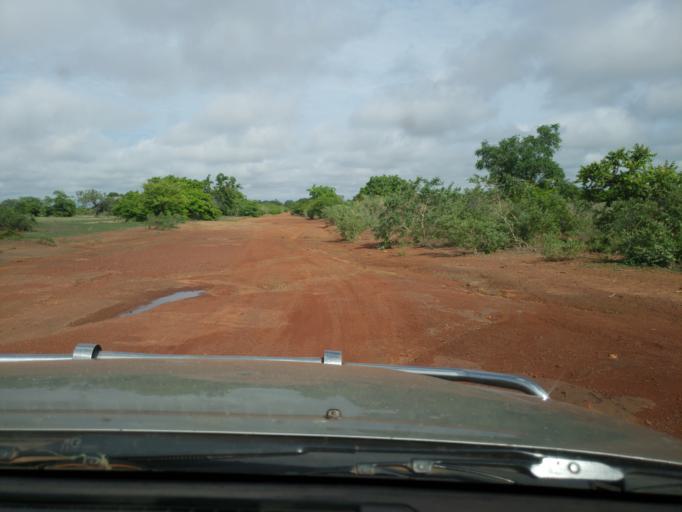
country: ML
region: Sikasso
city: Koutiala
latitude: 12.3924
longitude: -5.9960
